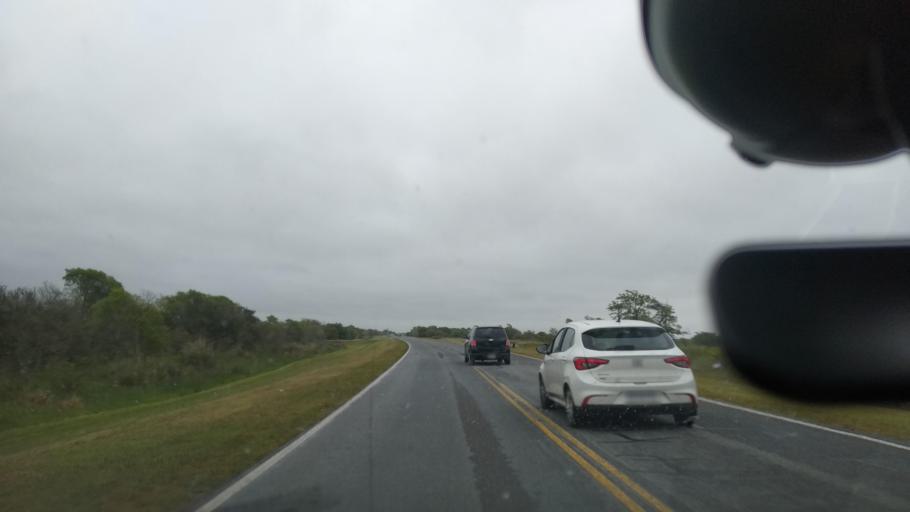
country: AR
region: Buenos Aires
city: Veronica
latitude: -35.7815
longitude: -57.3984
